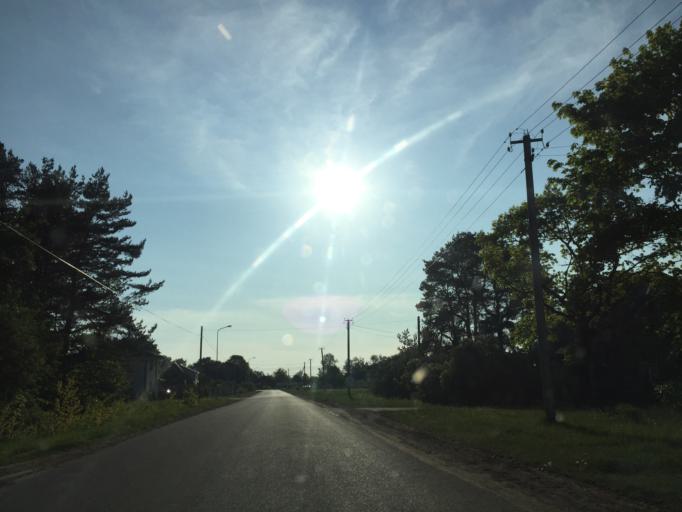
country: LV
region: Kekava
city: Kekava
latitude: 56.8257
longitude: 24.2594
